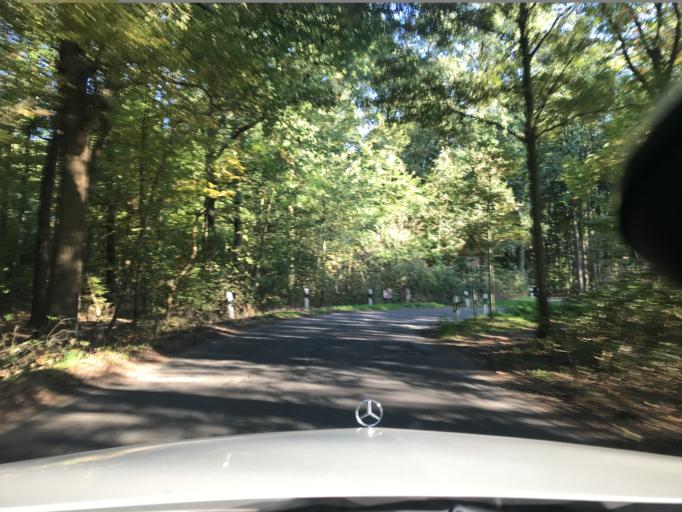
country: DE
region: North Rhine-Westphalia
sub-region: Regierungsbezirk Dusseldorf
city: Krefeld
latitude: 51.3585
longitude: 6.5492
